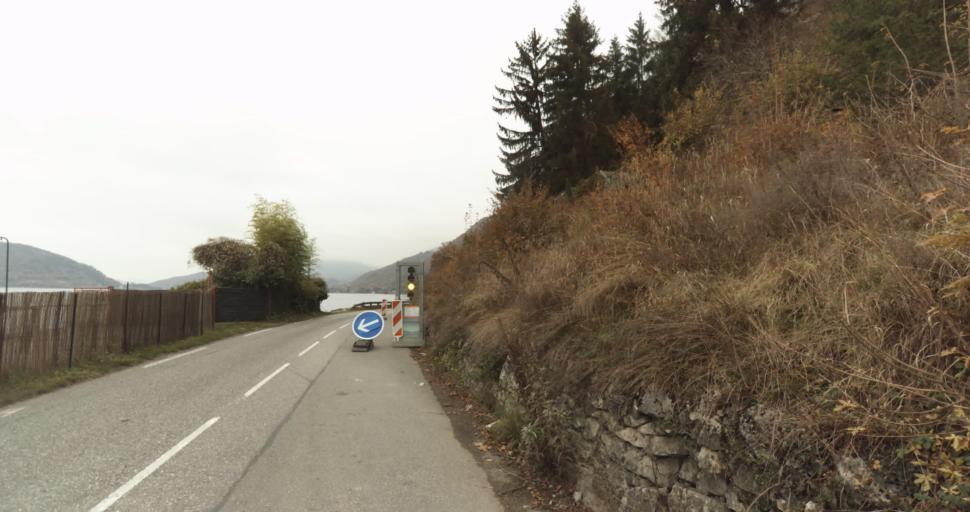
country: FR
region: Rhone-Alpes
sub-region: Departement de la Haute-Savoie
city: Doussard
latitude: 45.8064
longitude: 6.2322
